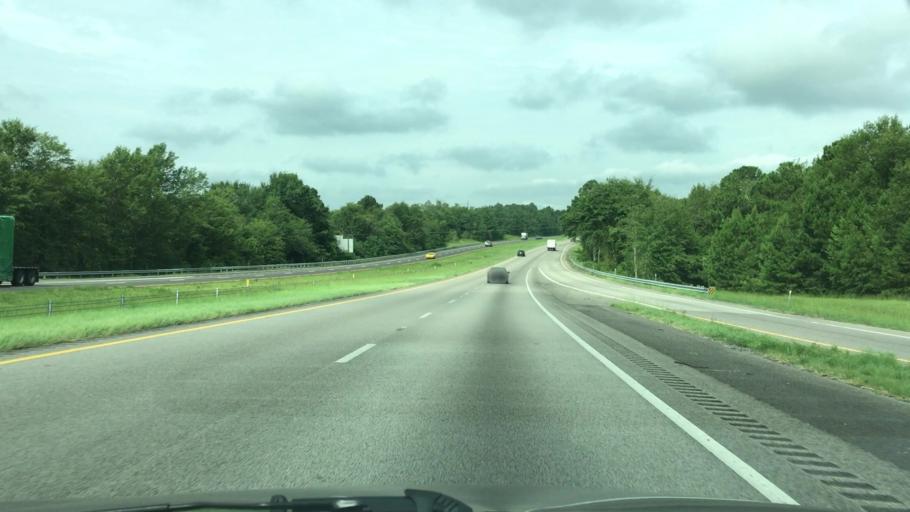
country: US
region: South Carolina
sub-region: Aiken County
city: Aiken
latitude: 33.6380
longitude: -81.7446
